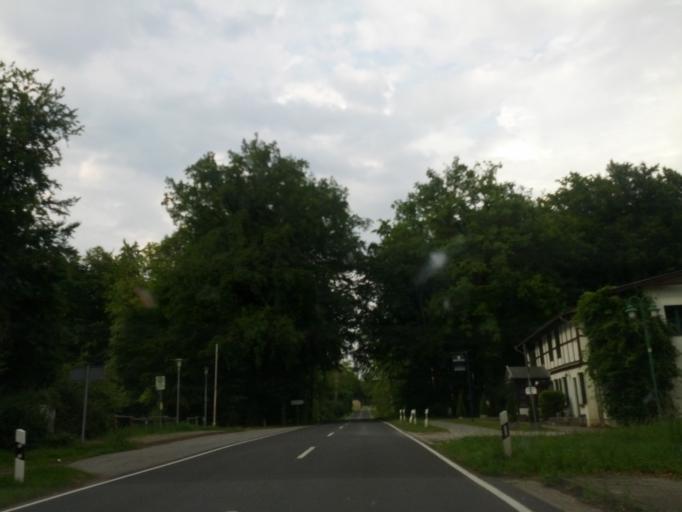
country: DE
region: Mecklenburg-Vorpommern
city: Kropelin
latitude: 54.0507
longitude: 11.7985
